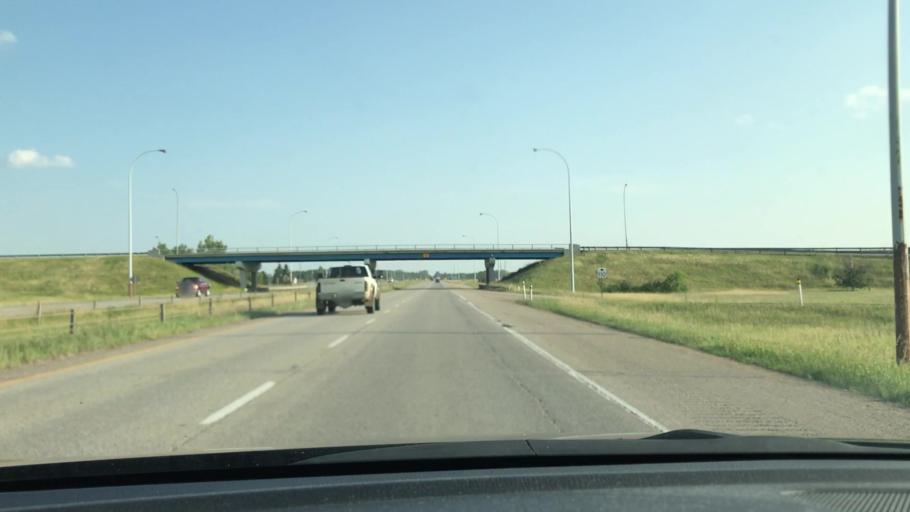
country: CA
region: Alberta
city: Leduc
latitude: 53.2541
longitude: -113.5619
